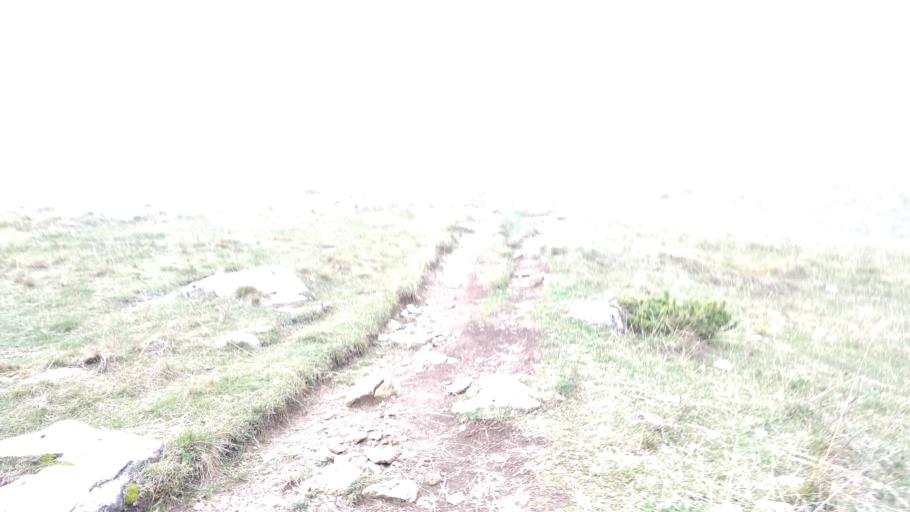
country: IT
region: Veneto
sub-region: Provincia di Vicenza
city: Roana
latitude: 45.9594
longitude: 11.4557
